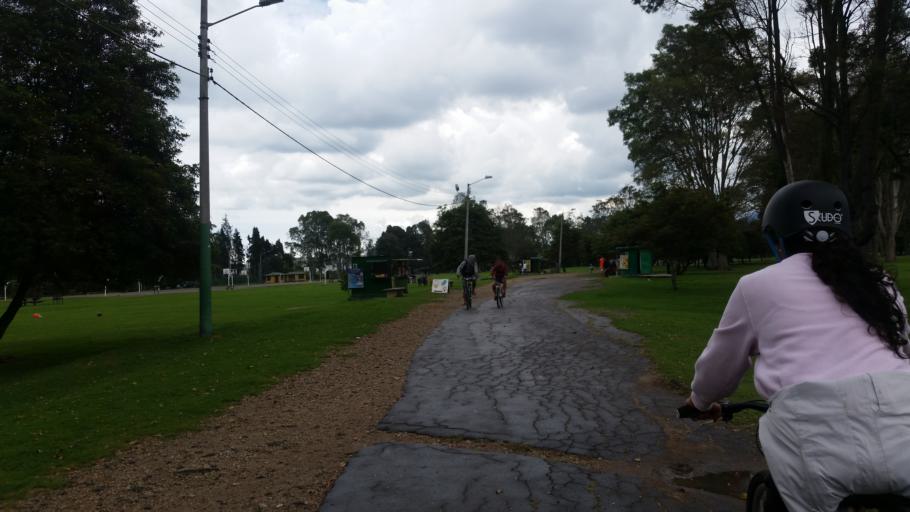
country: CO
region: Cundinamarca
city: Funza
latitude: 4.7309
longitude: -74.1463
